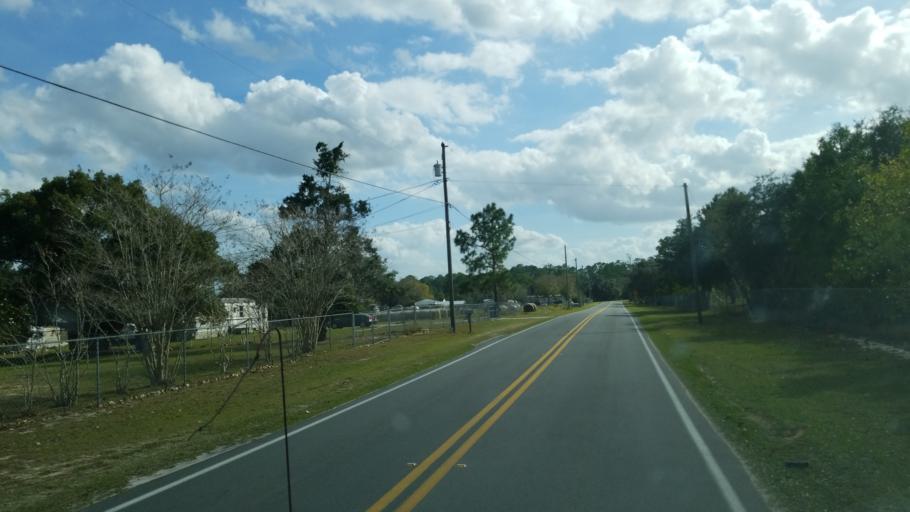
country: US
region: Florida
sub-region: Polk County
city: Davenport
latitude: 28.1503
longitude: -81.5657
